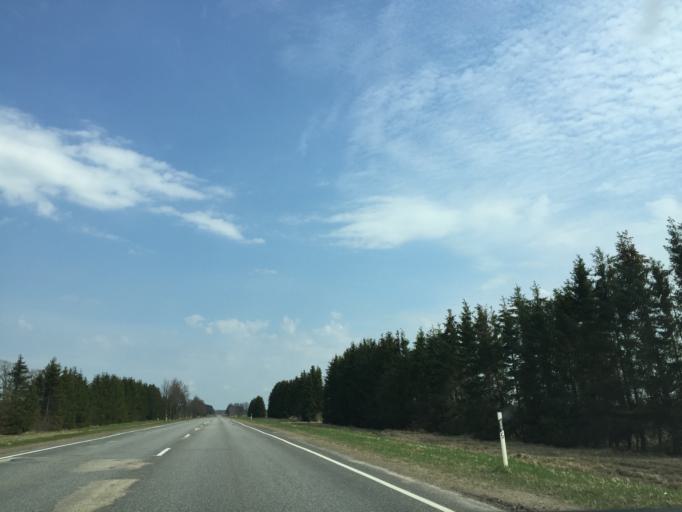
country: LV
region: Apes Novads
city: Ape
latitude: 57.4629
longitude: 26.4106
